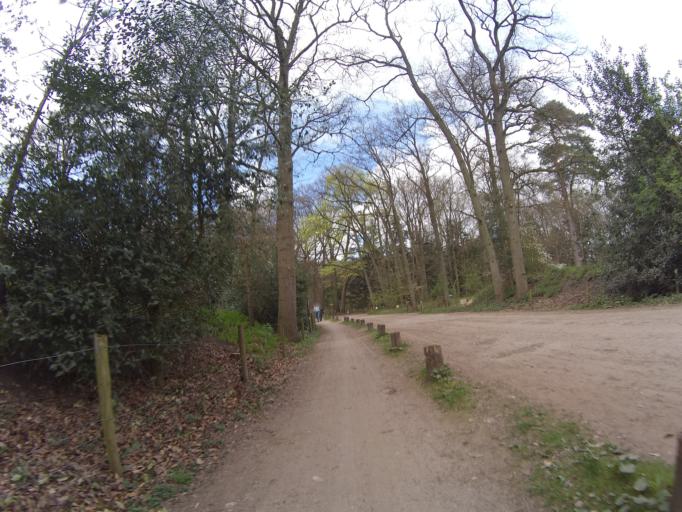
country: NL
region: North Holland
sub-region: Gemeente Hilversum
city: Hilversum
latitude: 52.2001
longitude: 5.2129
